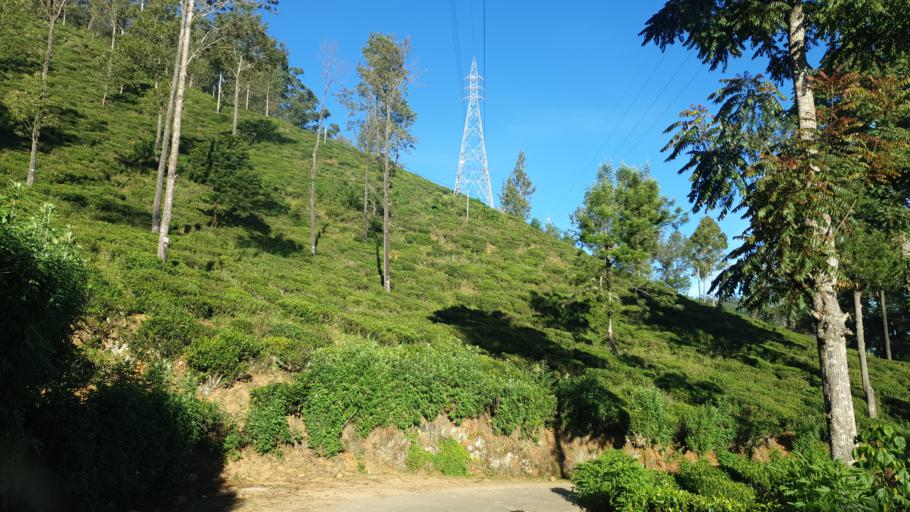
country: LK
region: Central
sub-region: Nuwara Eliya District
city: Nuwara Eliya
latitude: 6.9581
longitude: 80.7661
